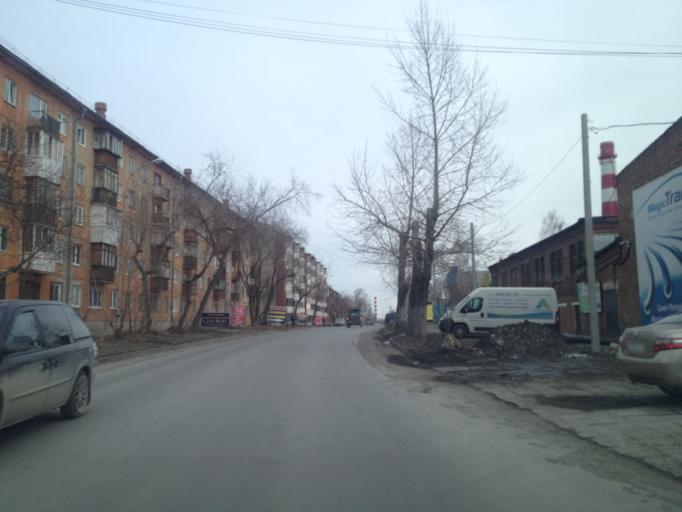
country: RU
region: Sverdlovsk
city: Shuvakish
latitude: 56.8669
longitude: 60.5257
